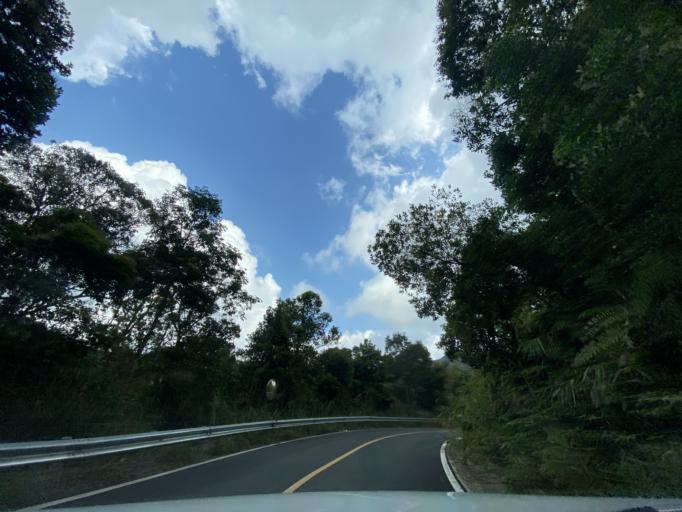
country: CN
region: Hainan
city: Diaoluoshan
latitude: 18.7097
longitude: 109.8828
